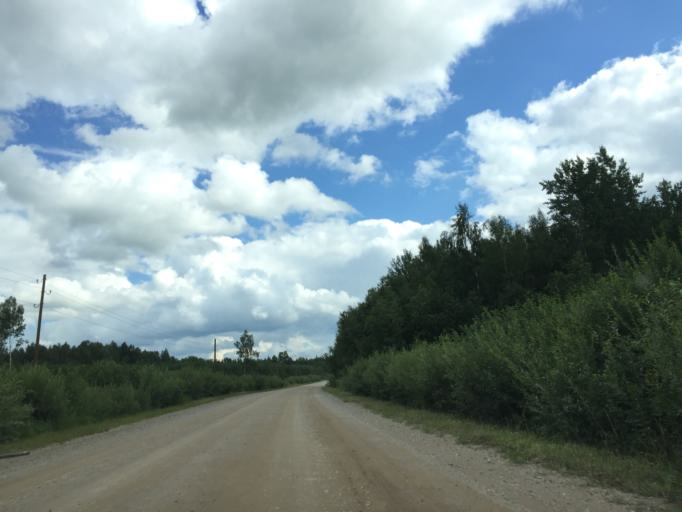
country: LV
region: Malpils
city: Malpils
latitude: 56.8785
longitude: 24.9954
